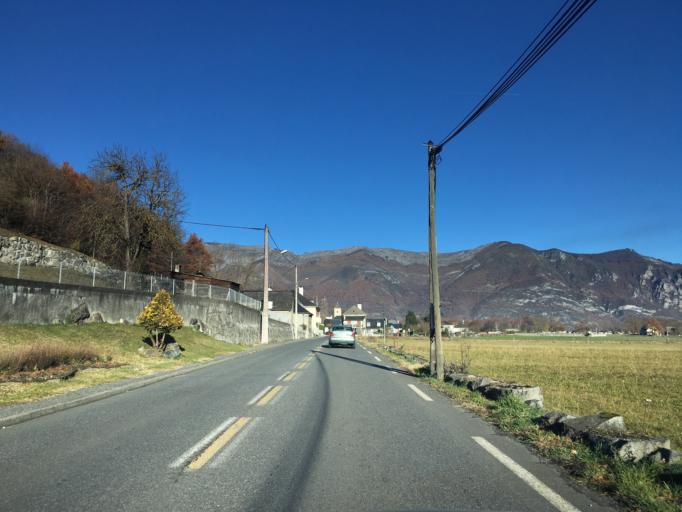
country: FR
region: Midi-Pyrenees
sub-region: Departement des Hautes-Pyrenees
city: Argeles-Gazost
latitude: 42.9932
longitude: -0.0910
